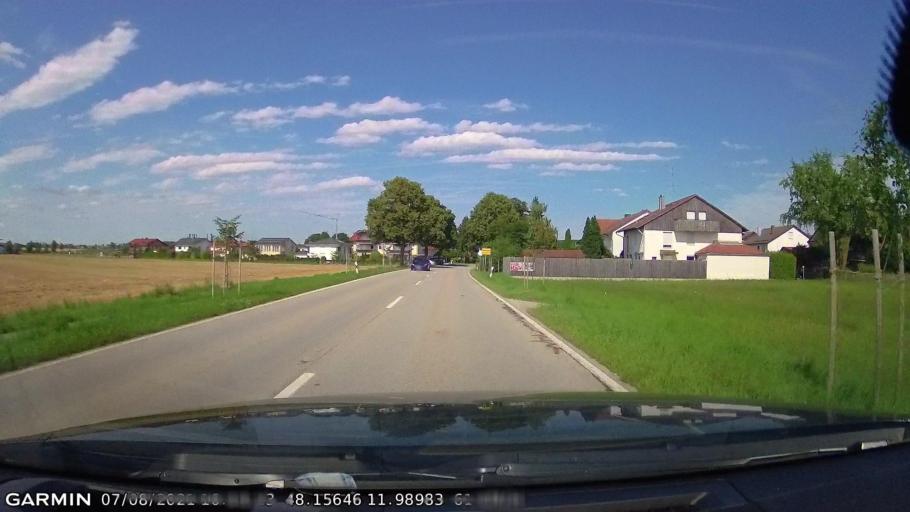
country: DE
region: Bavaria
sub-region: Upper Bavaria
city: Hohenlinden
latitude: 48.1564
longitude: 11.9898
